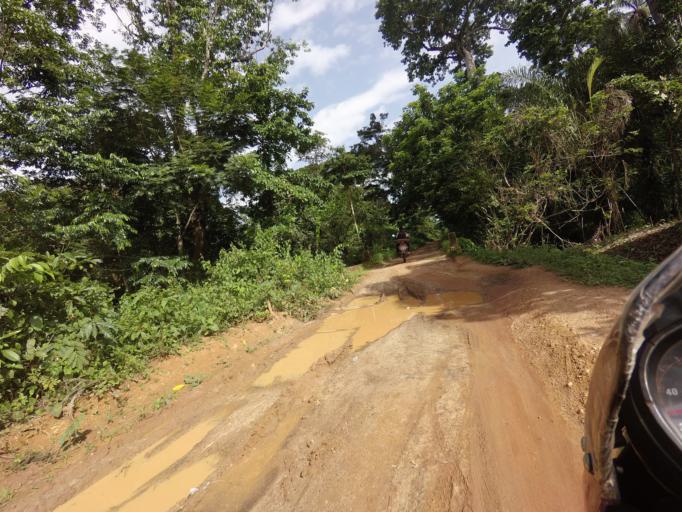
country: SL
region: Eastern Province
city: Jojoima
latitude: 7.8168
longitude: -10.8153
